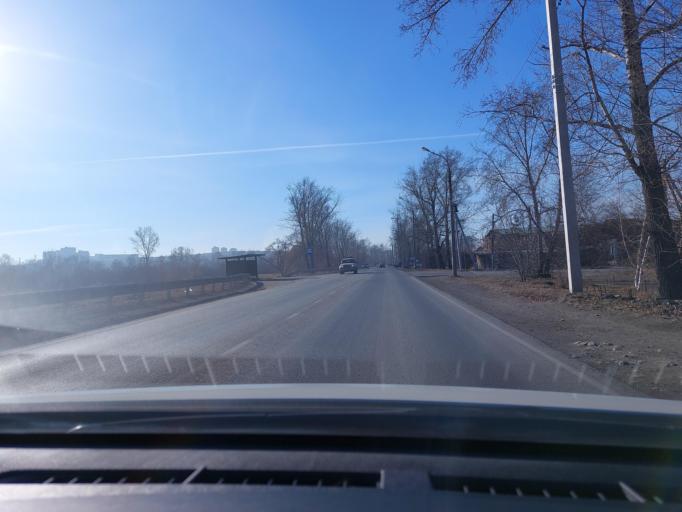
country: RU
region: Irkutsk
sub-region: Irkutskiy Rayon
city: Irkutsk
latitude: 52.3044
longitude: 104.2523
